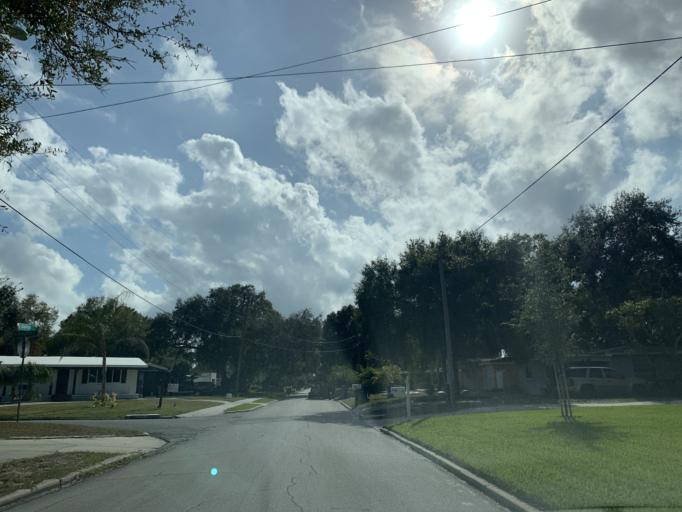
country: US
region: Florida
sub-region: Hillsborough County
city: Tampa
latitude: 27.9045
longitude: -82.5169
